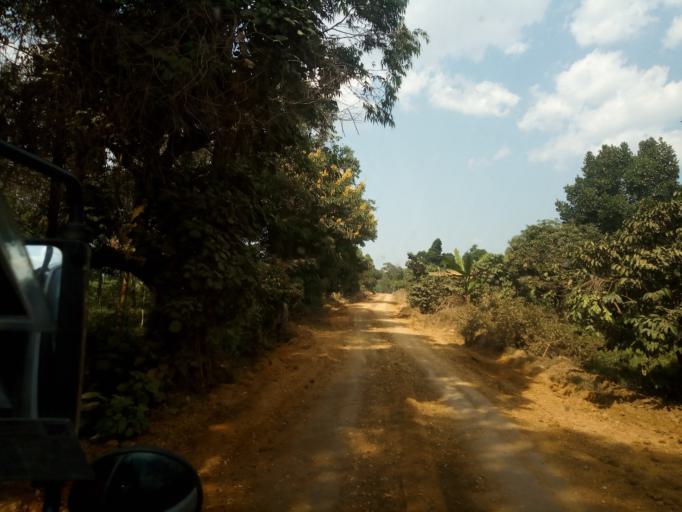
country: UG
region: Western Region
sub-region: Kanungu District
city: Ntungamo
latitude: -0.7833
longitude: 29.6947
